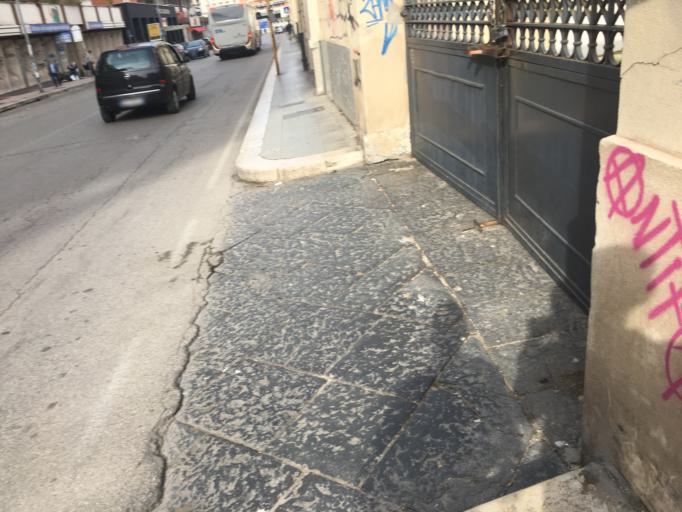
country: IT
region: Apulia
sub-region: Provincia di Bari
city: Bari
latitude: 41.1156
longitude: 16.8688
